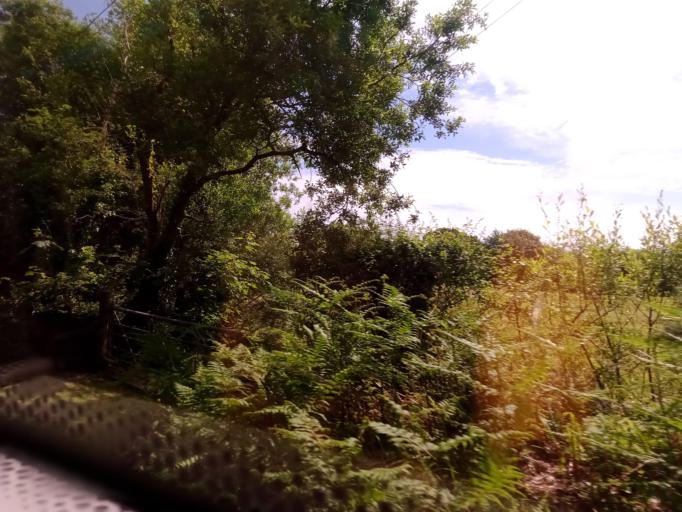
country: GB
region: Wales
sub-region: Gwynedd
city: Bangor
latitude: 53.2540
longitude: -4.1310
